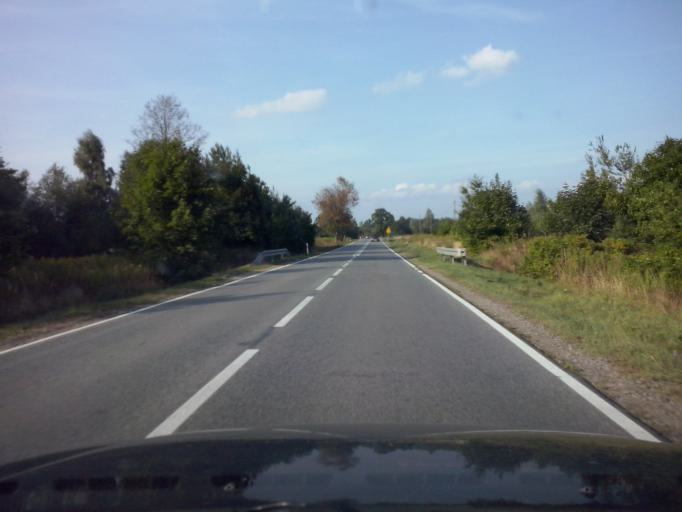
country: PL
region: Subcarpathian Voivodeship
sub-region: Powiat nizanski
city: Krzeszow
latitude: 50.3619
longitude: 22.3211
